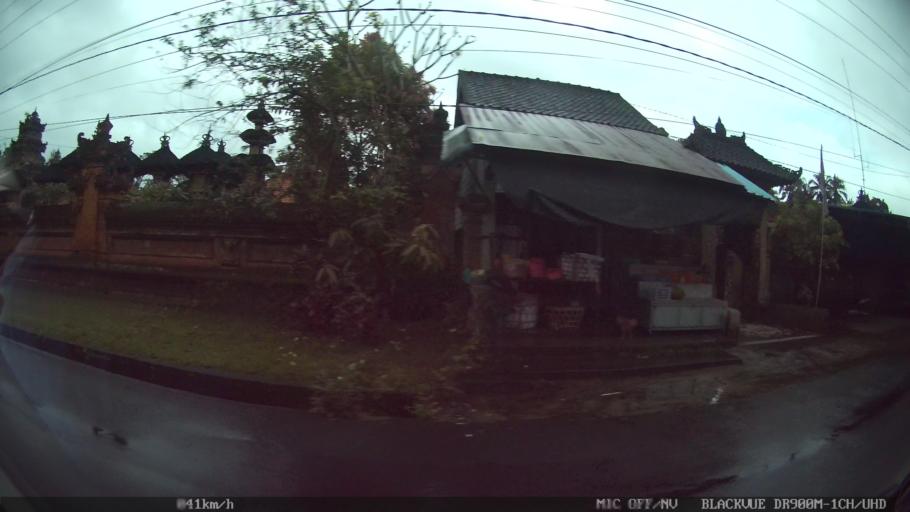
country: ID
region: Bali
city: Banjar Teguan
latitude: -8.5027
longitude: 115.2354
